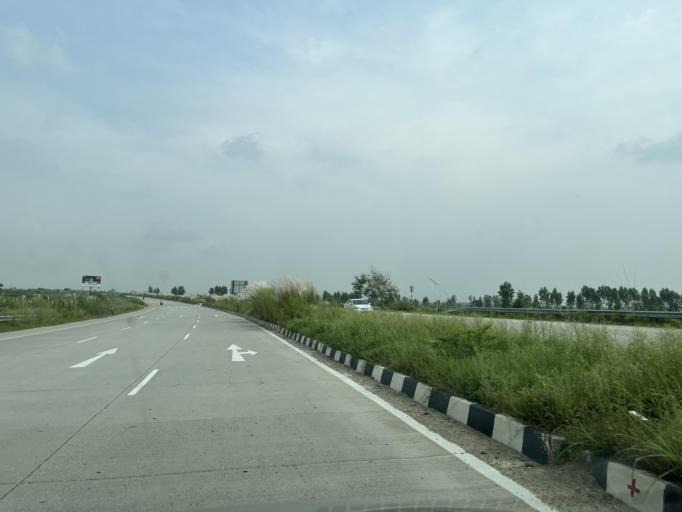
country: IN
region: Uttarakhand
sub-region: Udham Singh Nagar
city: Bazpur
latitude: 29.1487
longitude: 79.0257
